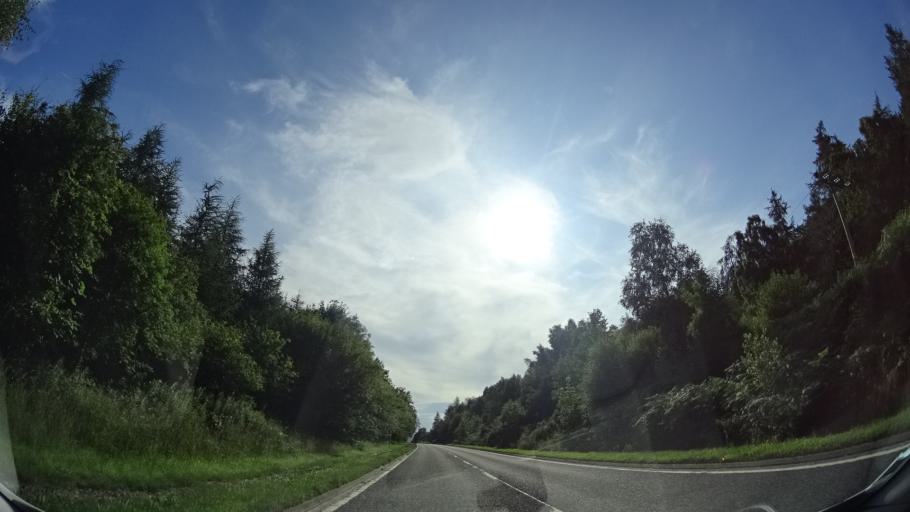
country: GB
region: Scotland
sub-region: Highland
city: Conon Bridge
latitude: 57.5650
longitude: -4.4800
